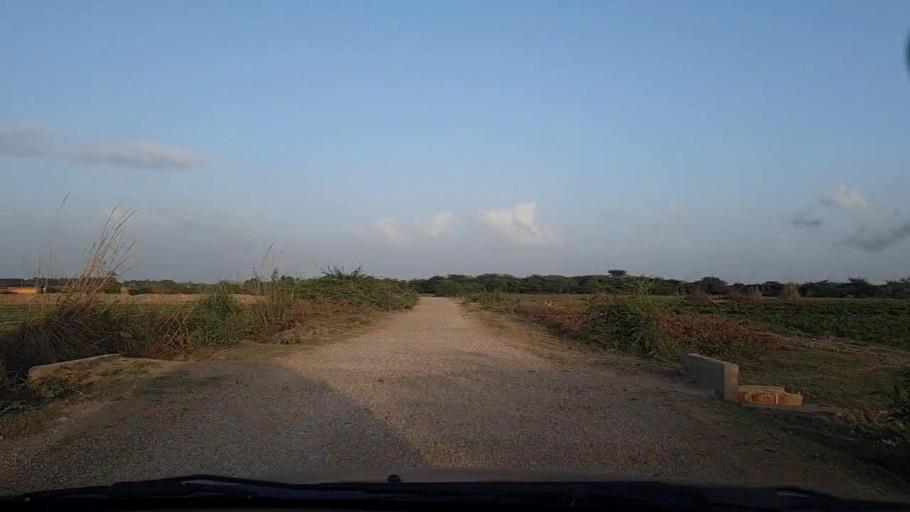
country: PK
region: Sindh
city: Keti Bandar
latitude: 24.1611
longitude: 67.5910
